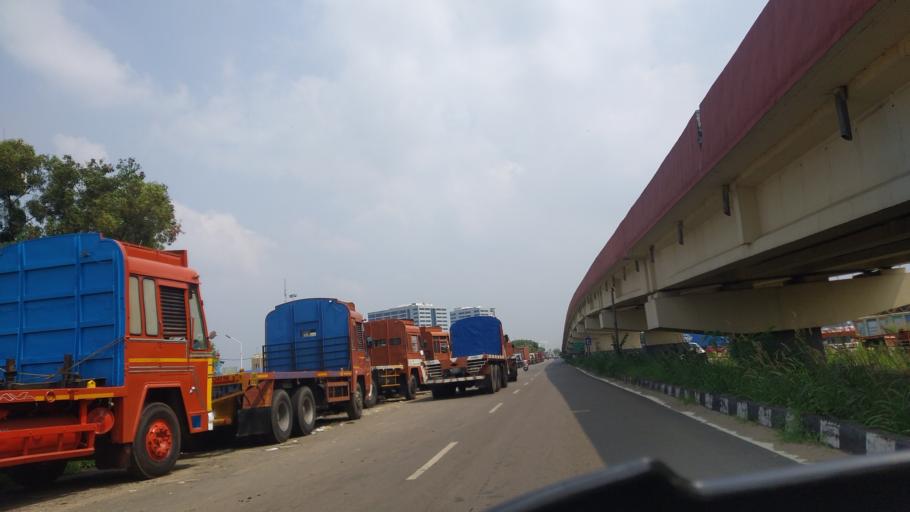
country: IN
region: Kerala
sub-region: Ernakulam
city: Cochin
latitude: 9.9848
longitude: 76.2472
